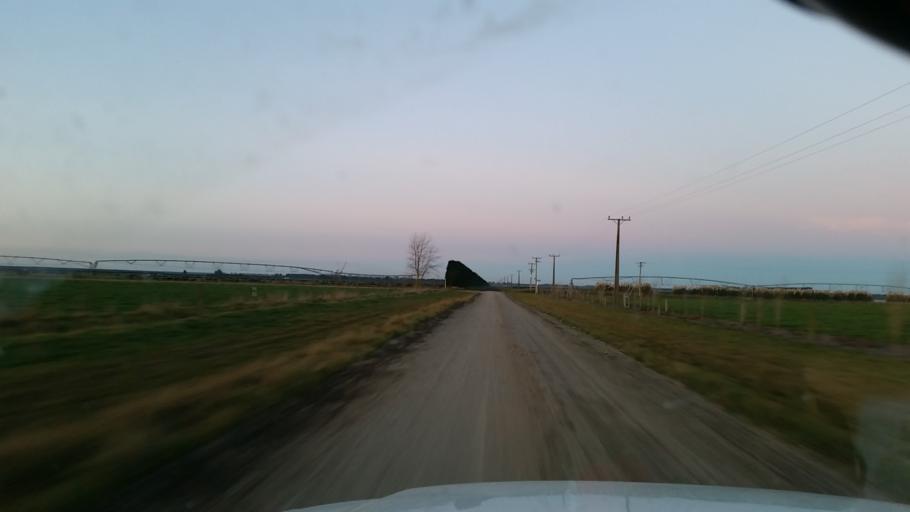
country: NZ
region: Canterbury
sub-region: Ashburton District
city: Tinwald
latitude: -43.9385
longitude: 171.5606
